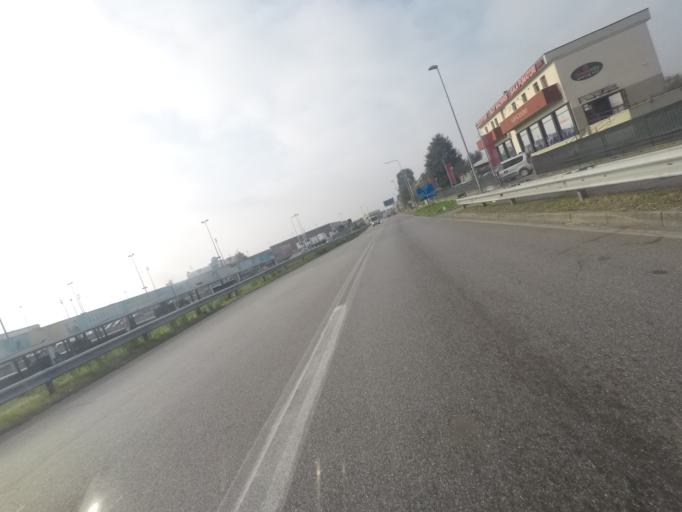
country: IT
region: Lombardy
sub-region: Provincia di Monza e Brianza
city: Concorezzo
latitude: 45.5824
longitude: 9.3269
